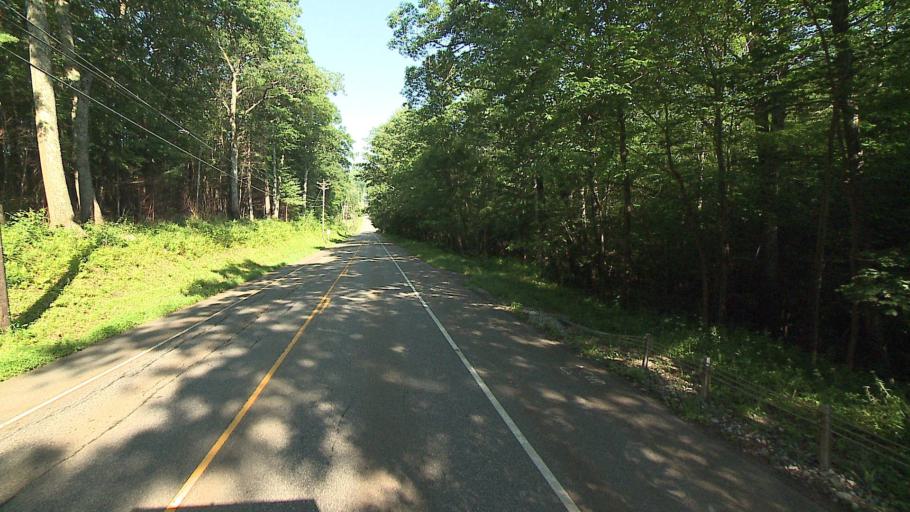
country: US
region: Connecticut
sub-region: Litchfield County
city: Litchfield
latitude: 41.8441
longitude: -73.3031
